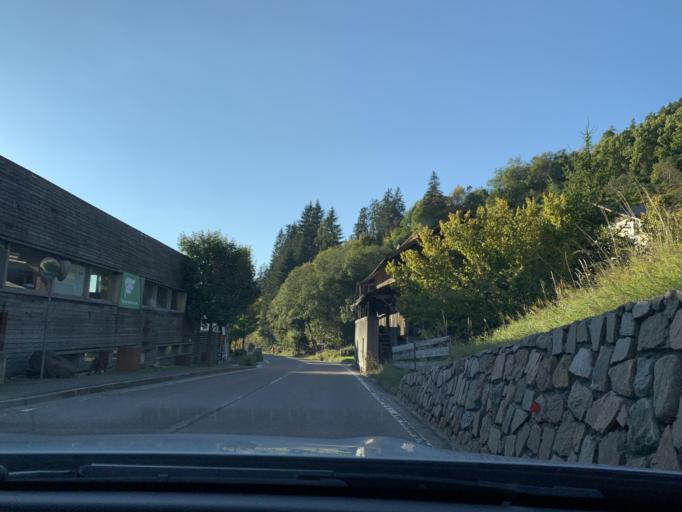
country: IT
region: Trentino-Alto Adige
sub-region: Bolzano
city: Nova Levante
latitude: 46.4276
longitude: 11.5342
